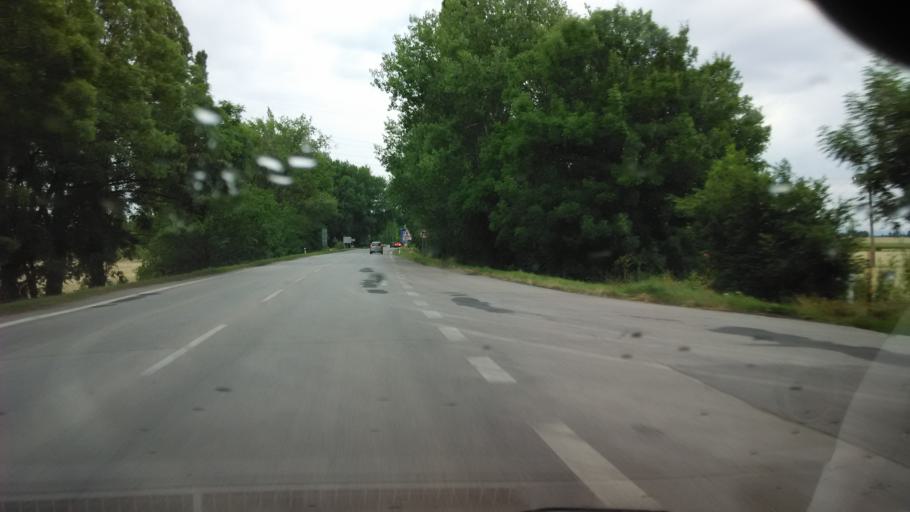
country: SK
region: Trnavsky
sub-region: Okres Trnava
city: Trnava
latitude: 48.3491
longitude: 17.5715
